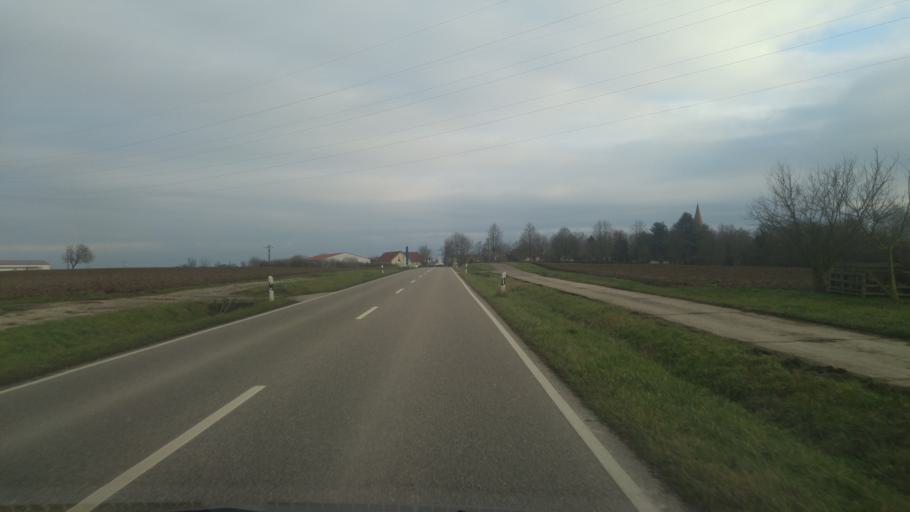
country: DE
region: Rheinland-Pfalz
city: Minfeld
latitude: 49.0757
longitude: 8.1354
